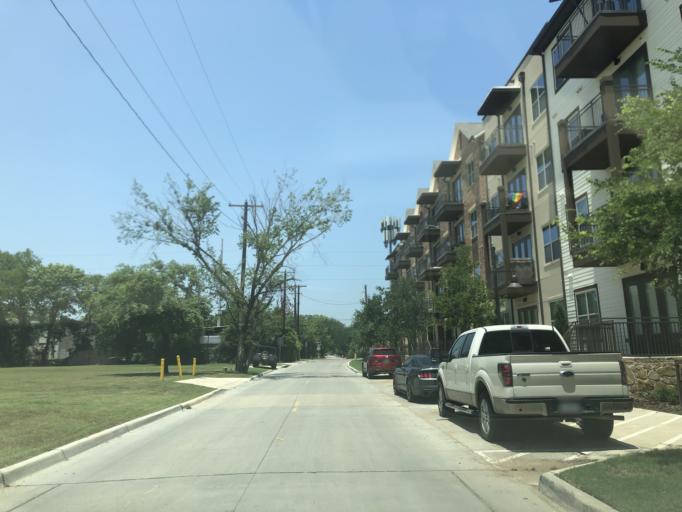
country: US
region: Texas
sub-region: Dallas County
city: Dallas
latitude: 32.7775
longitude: -96.8422
